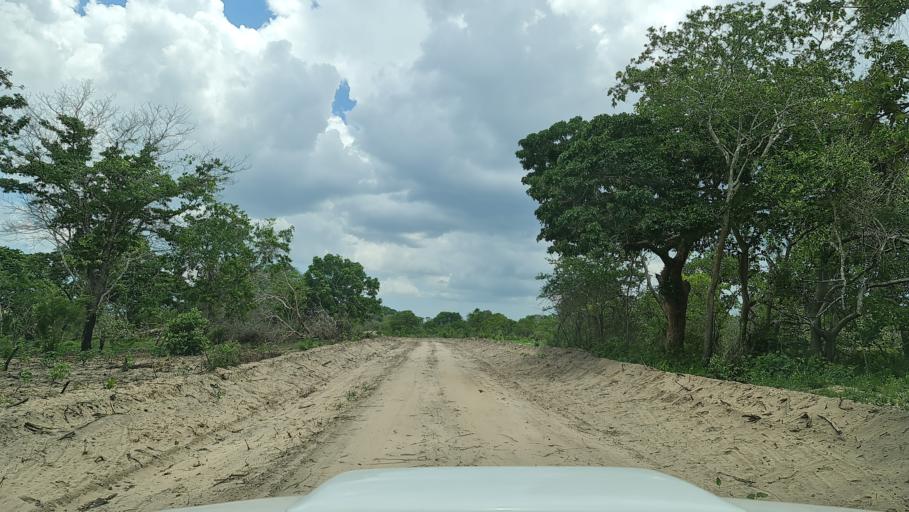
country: MZ
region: Nampula
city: Ilha de Mocambique
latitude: -15.2460
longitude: 40.3657
